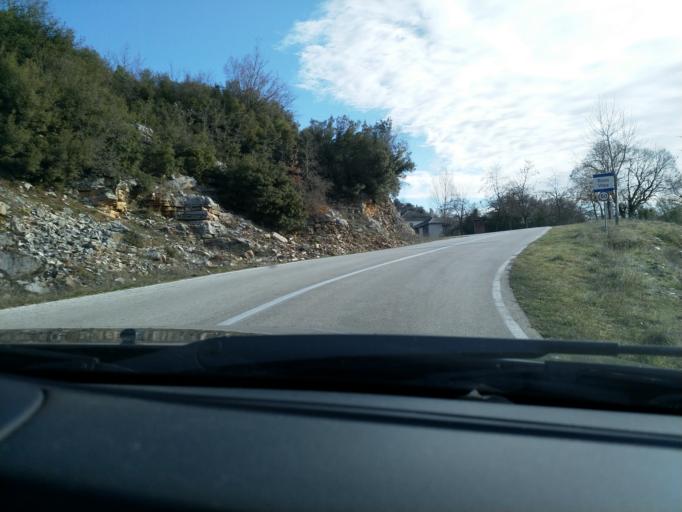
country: GR
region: Epirus
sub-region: Nomos Ioanninon
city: Asprangeloi
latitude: 39.8723
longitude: 20.7446
